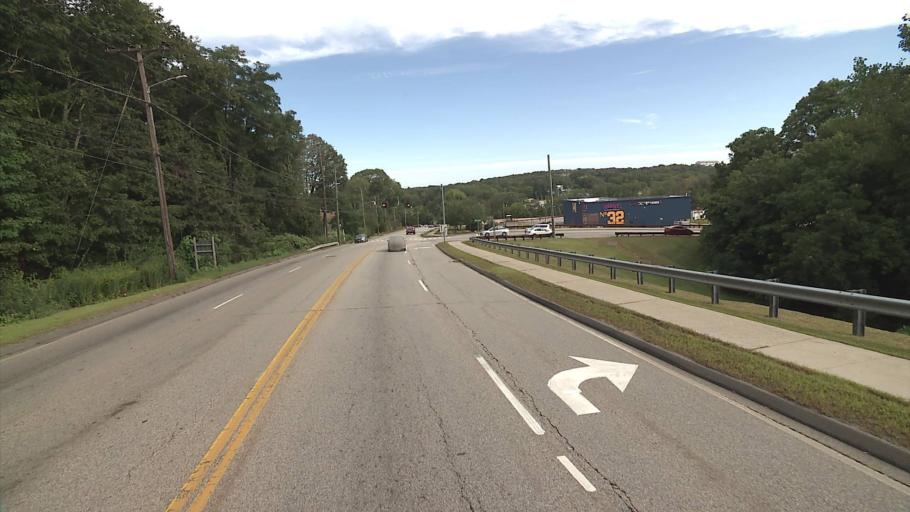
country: US
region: Connecticut
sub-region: New London County
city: Norwich
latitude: 41.4920
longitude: -72.1000
